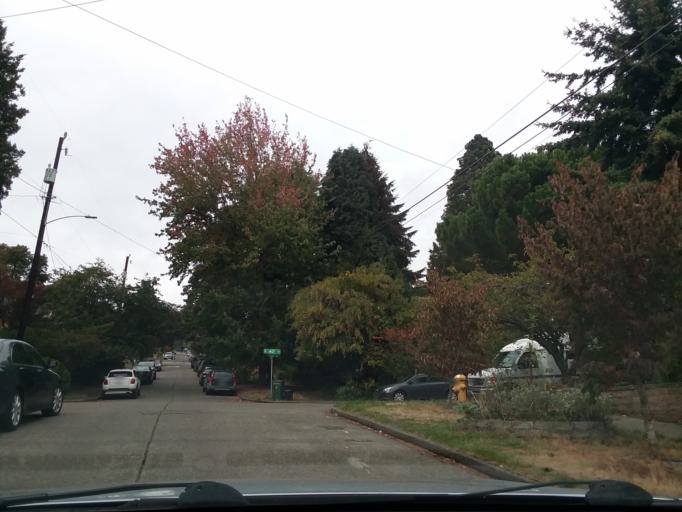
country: US
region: Washington
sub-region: King County
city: Seattle
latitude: 47.6552
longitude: -122.3526
